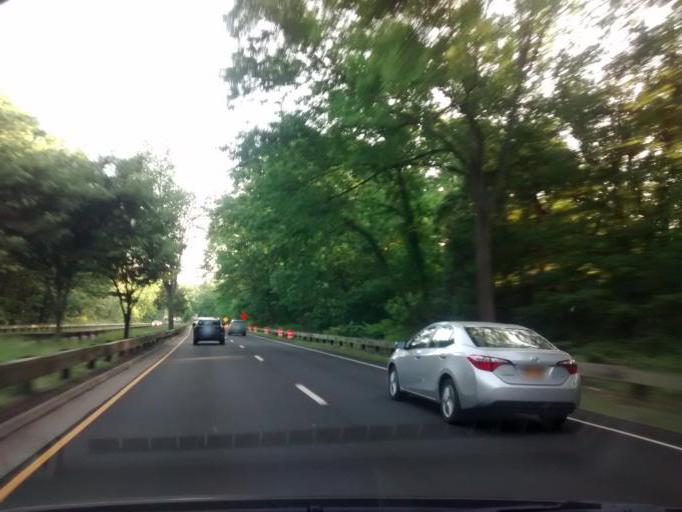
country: US
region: Connecticut
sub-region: Fairfield County
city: Glenville
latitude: 41.0894
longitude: -73.6597
